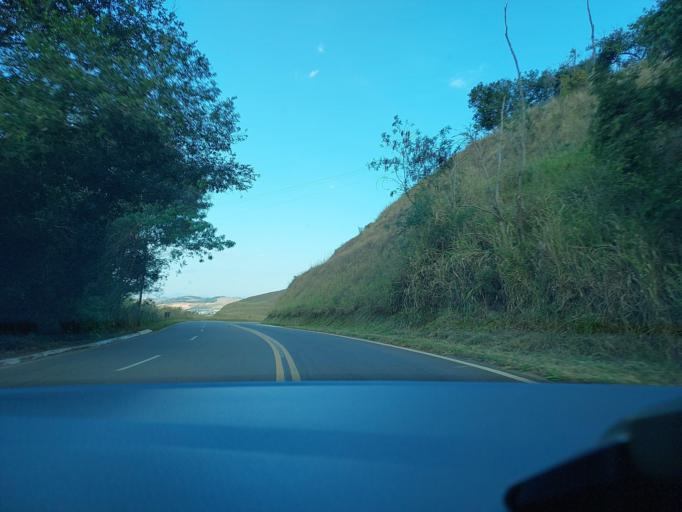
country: BR
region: Minas Gerais
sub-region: Muriae
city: Muriae
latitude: -21.0949
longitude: -42.4723
